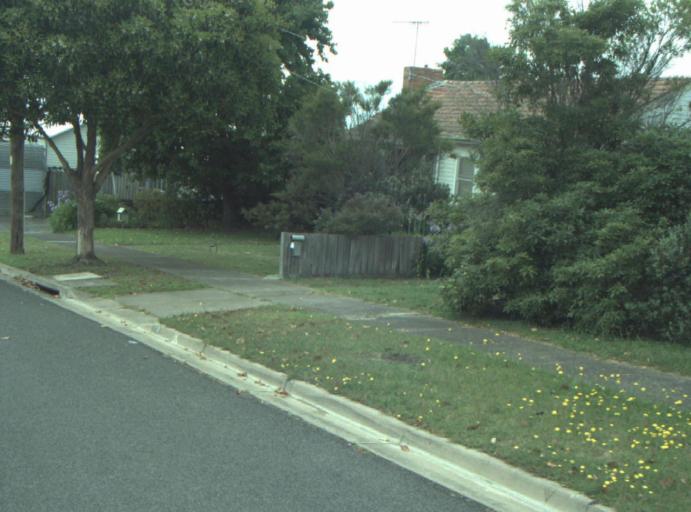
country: AU
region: Victoria
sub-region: Greater Geelong
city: Breakwater
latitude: -38.1689
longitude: 144.3444
